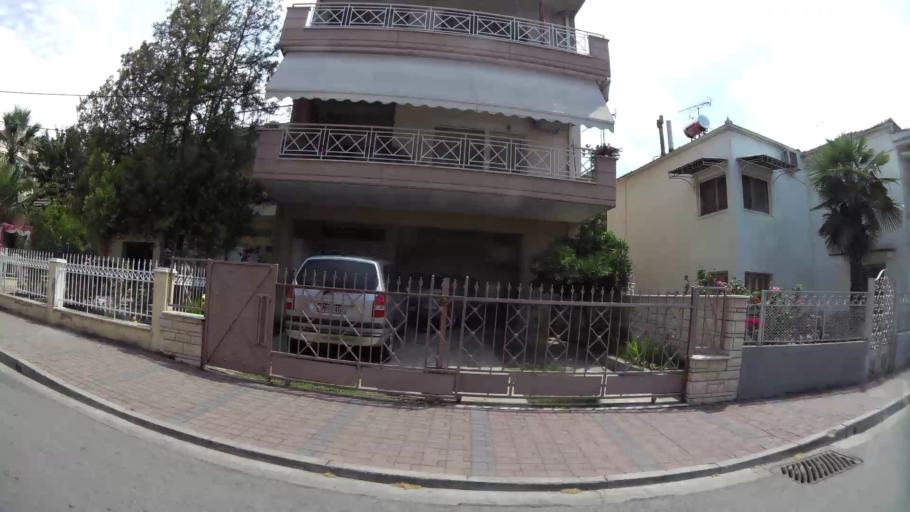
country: GR
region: Central Macedonia
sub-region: Nomos Pierias
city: Katerini
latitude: 40.2660
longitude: 22.5055
